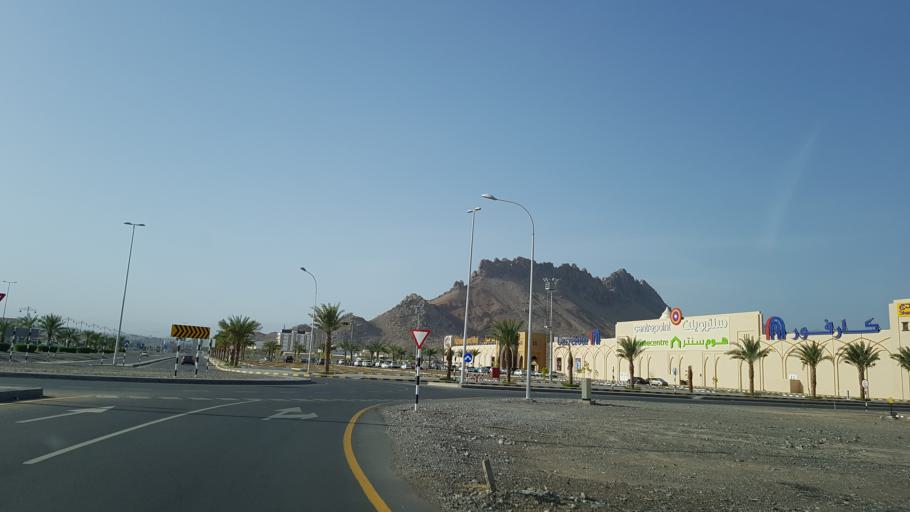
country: OM
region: Muhafazat ad Dakhiliyah
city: Nizwa
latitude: 22.8693
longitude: 57.5370
